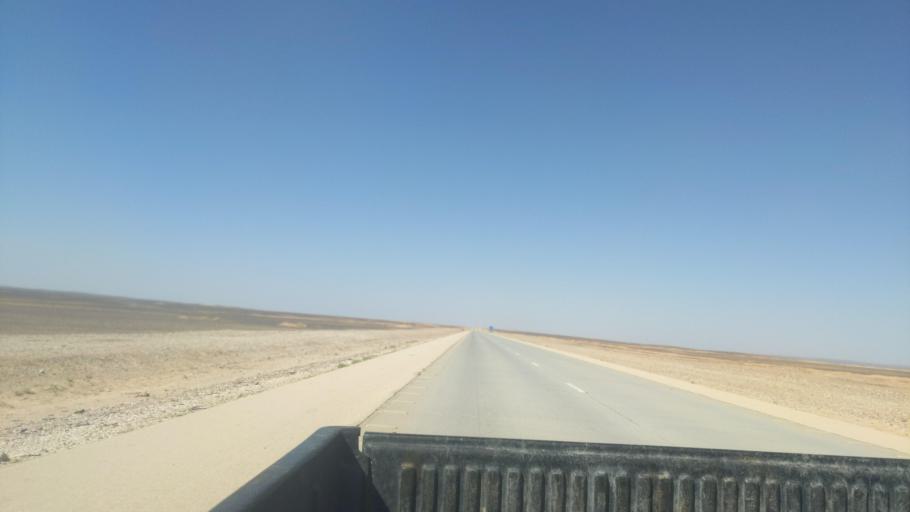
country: JO
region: Amman
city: Al Azraq ash Shamali
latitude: 31.4440
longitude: 36.7594
